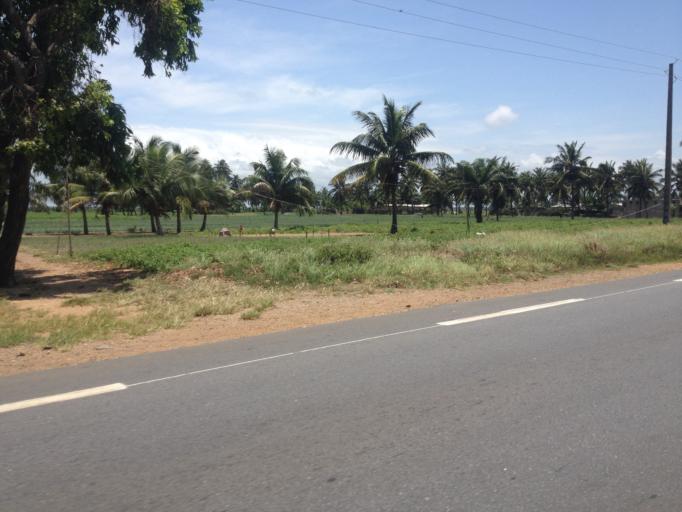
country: BJ
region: Mono
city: Grand-Popo
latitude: 6.2683
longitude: 1.7754
